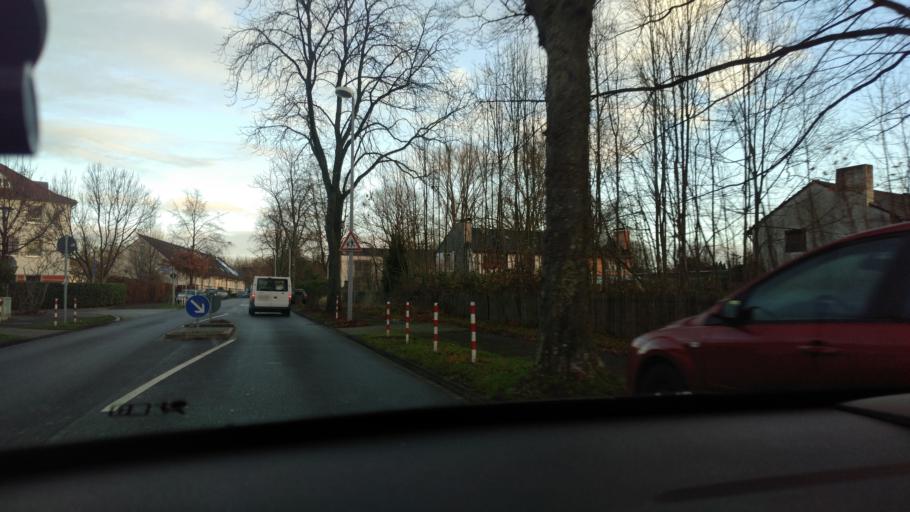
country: DE
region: North Rhine-Westphalia
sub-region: Regierungsbezirk Dusseldorf
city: Muelheim (Ruhr)
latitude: 51.4117
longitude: 6.9065
